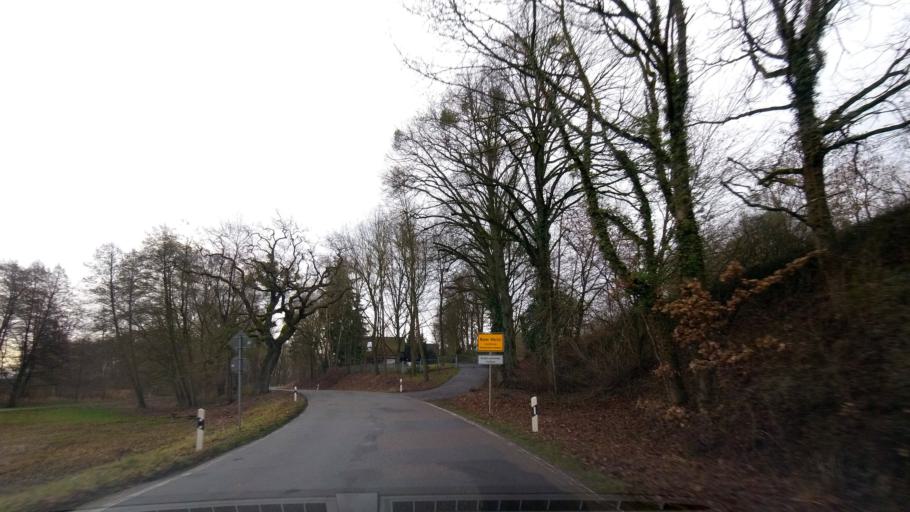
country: DE
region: Mecklenburg-Vorpommern
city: Waren
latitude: 53.5333
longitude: 12.6850
